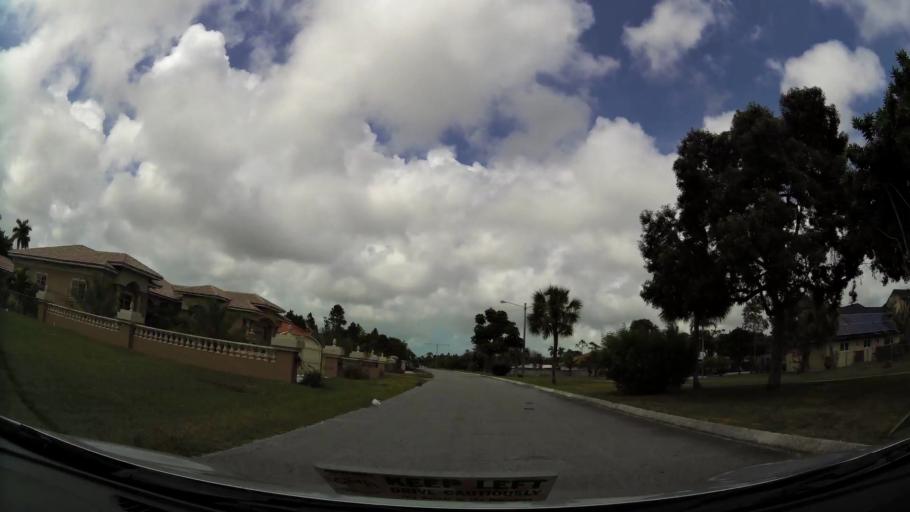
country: BS
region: Freeport
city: Freeport
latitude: 26.5139
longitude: -78.7081
